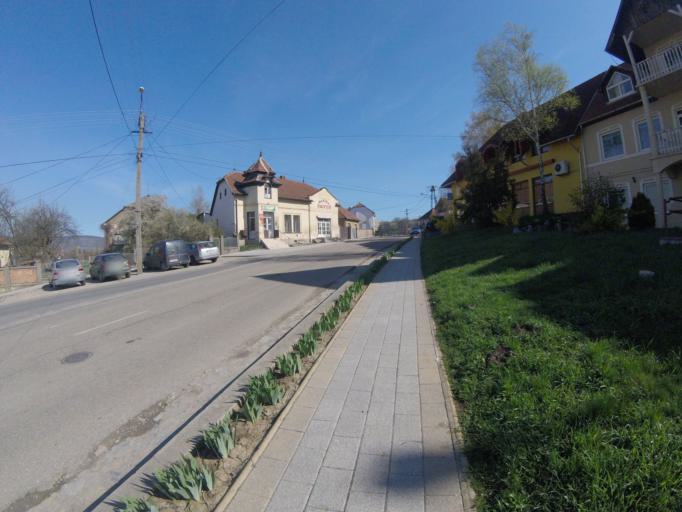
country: HU
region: Borsod-Abauj-Zemplen
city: Szendro
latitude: 48.4075
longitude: 20.7290
